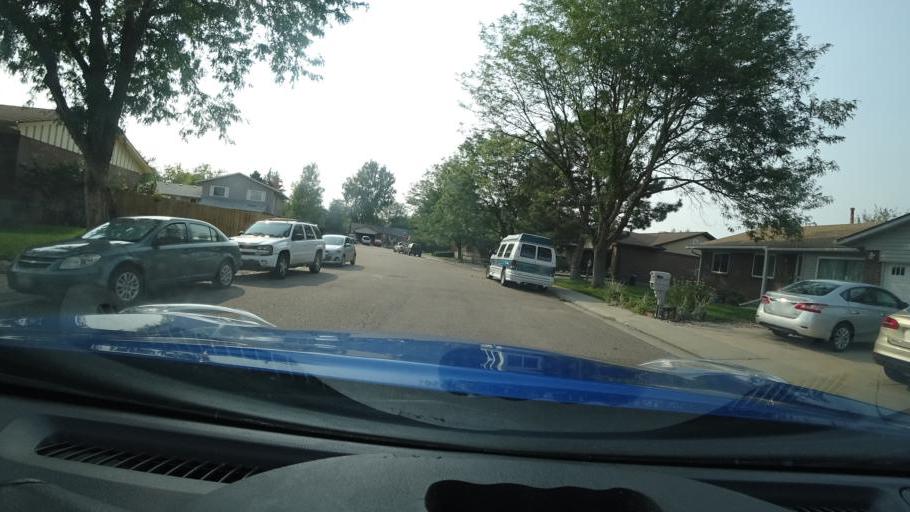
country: US
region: Colorado
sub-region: Adams County
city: Aurora
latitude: 39.6694
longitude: -104.7837
